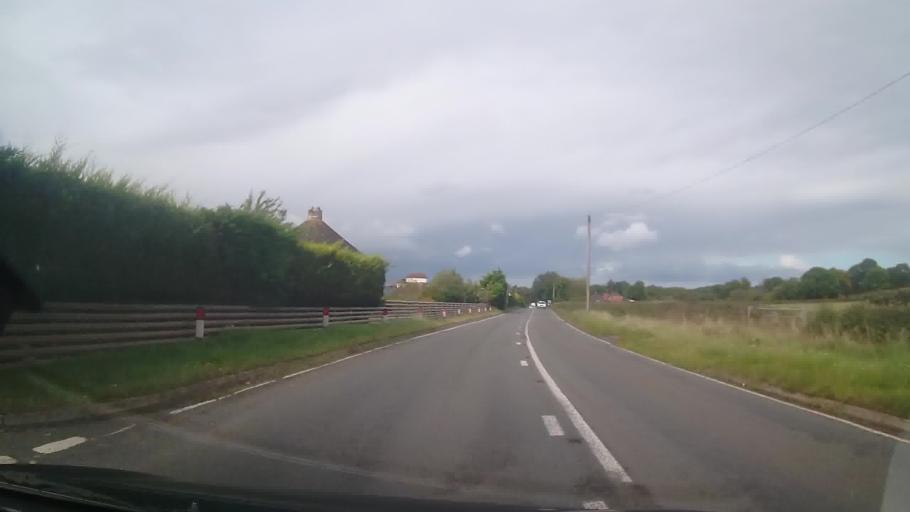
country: GB
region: England
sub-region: Shropshire
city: Alveley
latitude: 52.4471
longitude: -2.3373
